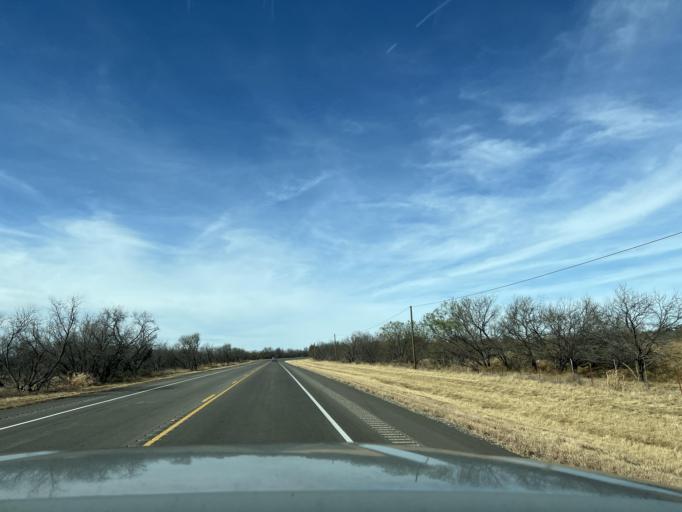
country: US
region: Texas
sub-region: Shackelford County
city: Albany
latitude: 32.5762
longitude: -99.1803
